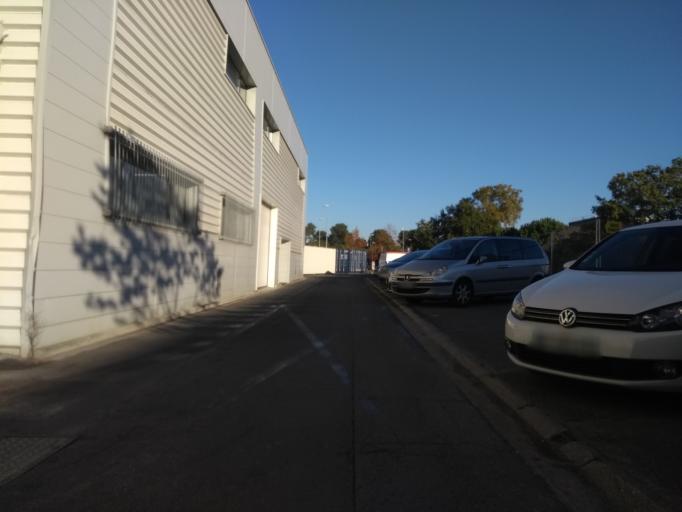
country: FR
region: Aquitaine
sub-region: Departement de la Gironde
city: Talence
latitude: 44.8029
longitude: -0.6098
